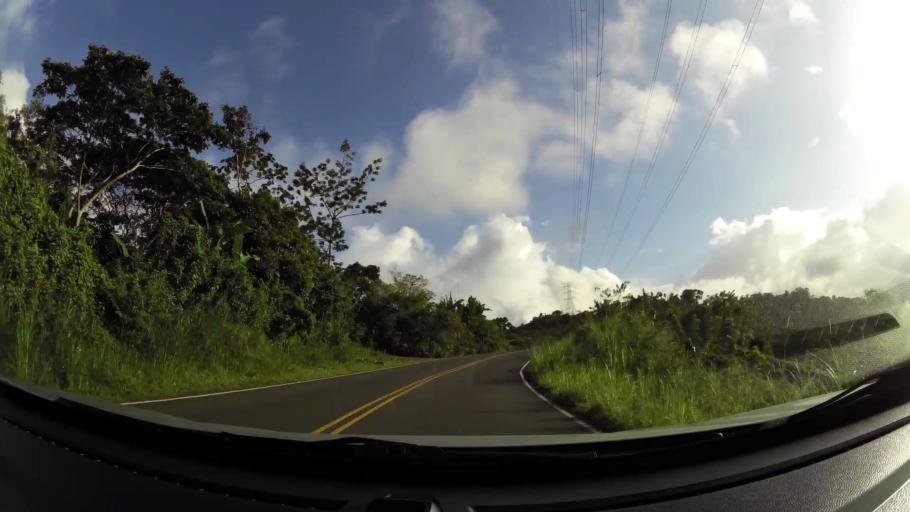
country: CR
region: Limon
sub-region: Canton de Siquirres
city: Siquirres
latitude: 10.0424
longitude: -83.5485
